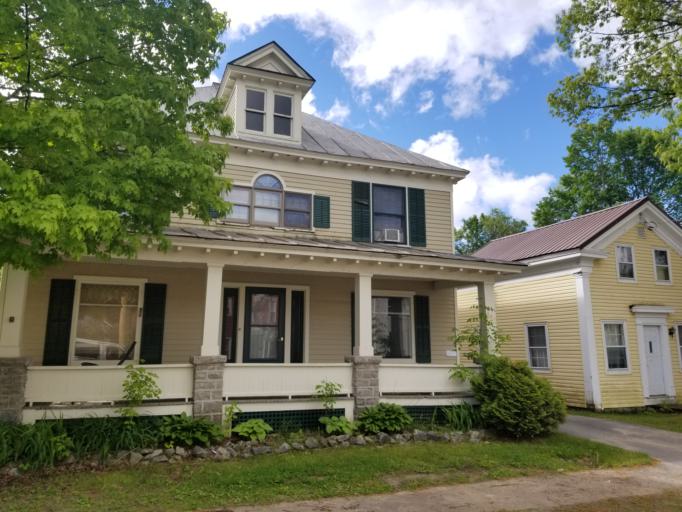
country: US
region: New York
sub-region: Oneida County
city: Utica
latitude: 43.3063
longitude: -75.1486
